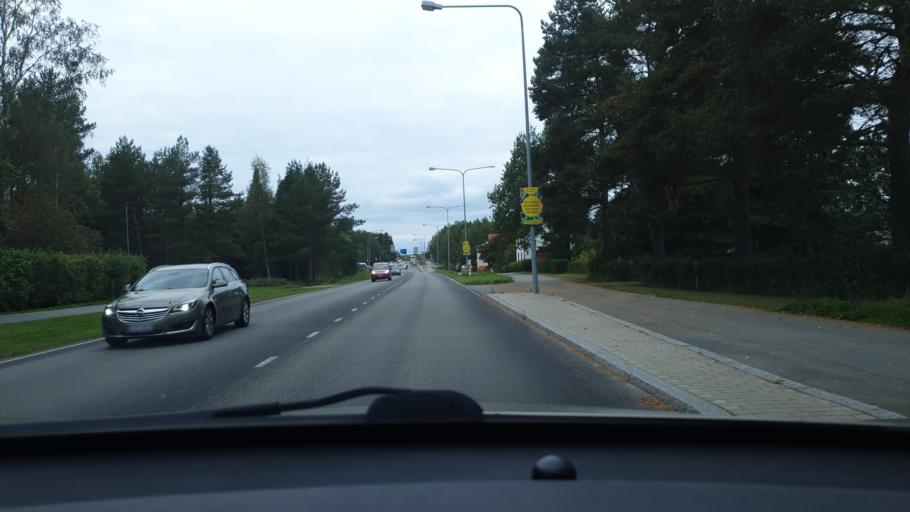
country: FI
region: Ostrobothnia
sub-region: Vaasa
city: Teeriniemi
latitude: 63.0903
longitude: 21.6711
